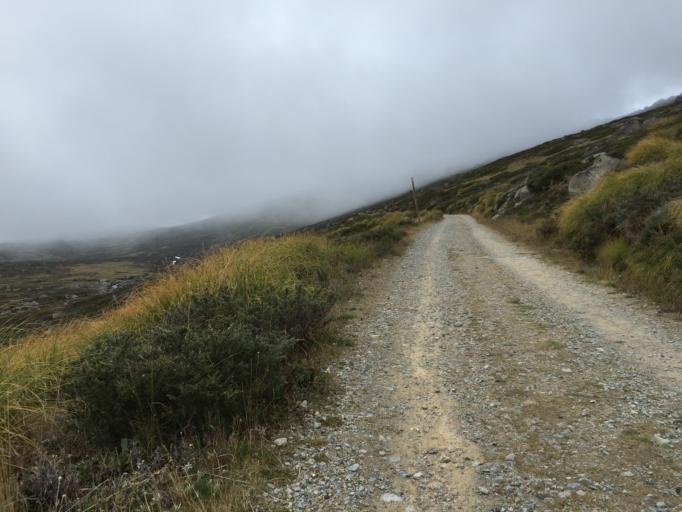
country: AU
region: New South Wales
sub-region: Snowy River
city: Jindabyne
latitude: -36.4538
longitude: 148.3044
